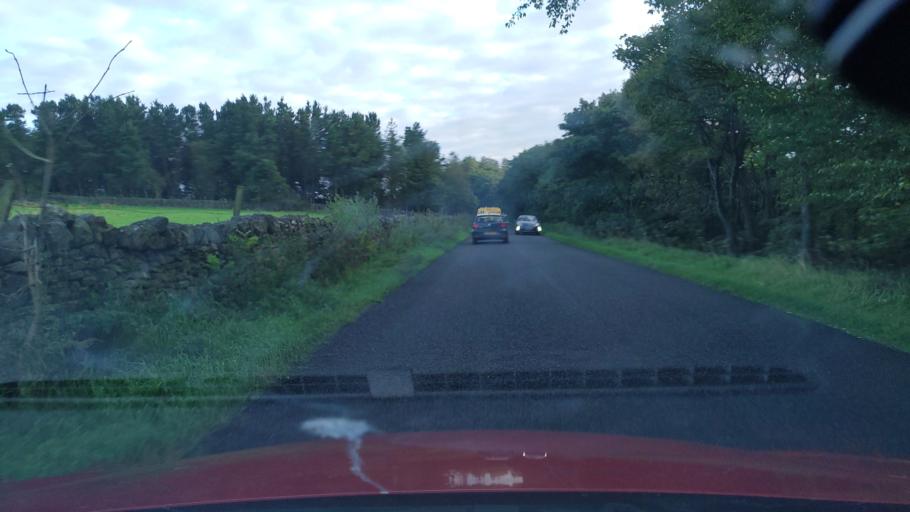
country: GB
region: England
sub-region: Blackburn with Darwen
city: Darwen
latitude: 53.6828
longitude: -2.5098
